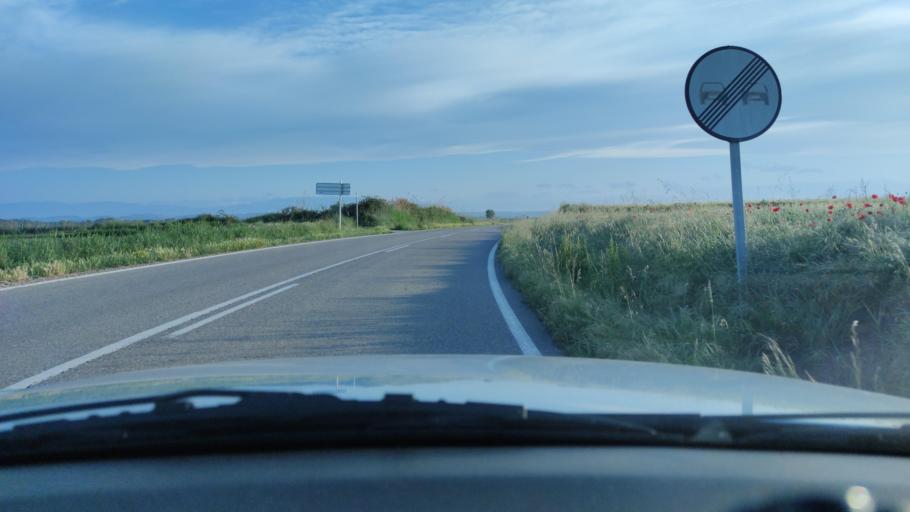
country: ES
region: Catalonia
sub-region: Provincia de Lleida
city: Ivars d'Urgell
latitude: 41.7037
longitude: 0.9816
